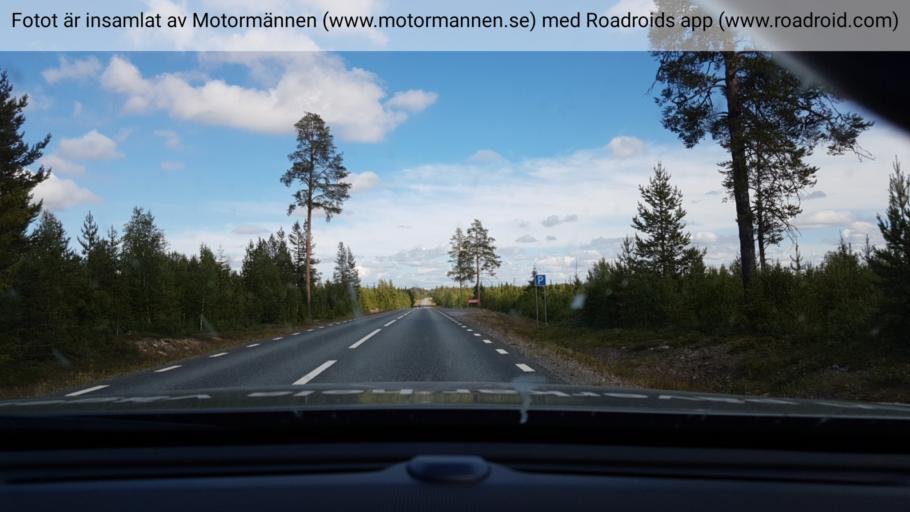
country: SE
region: Vaesterbotten
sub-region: Sorsele Kommun
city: Sorsele
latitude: 65.5572
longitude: 17.8823
